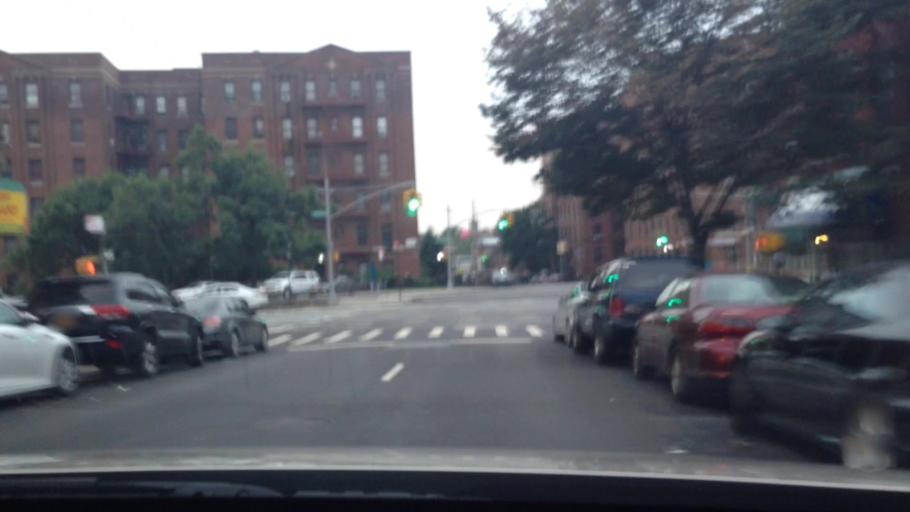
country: US
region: New York
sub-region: Kings County
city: Brooklyn
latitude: 40.6639
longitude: -73.9344
